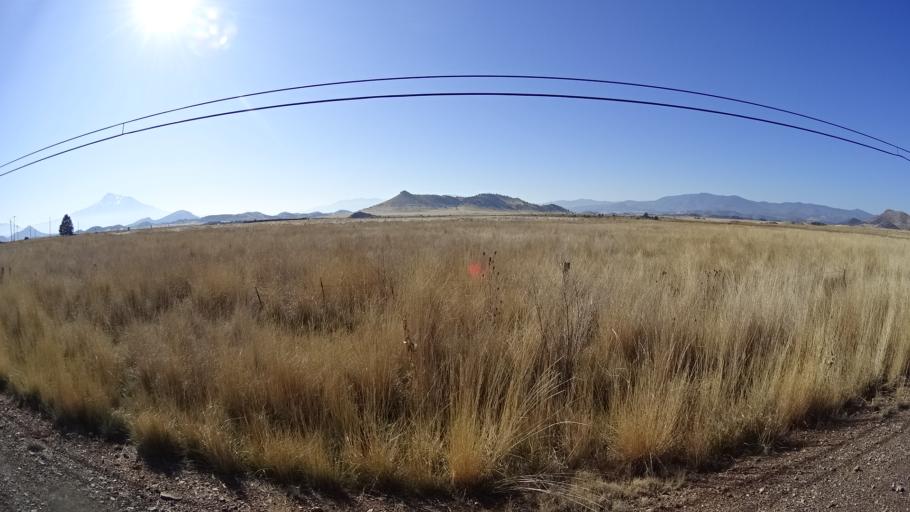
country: US
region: California
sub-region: Siskiyou County
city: Montague
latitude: 41.7265
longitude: -122.4591
